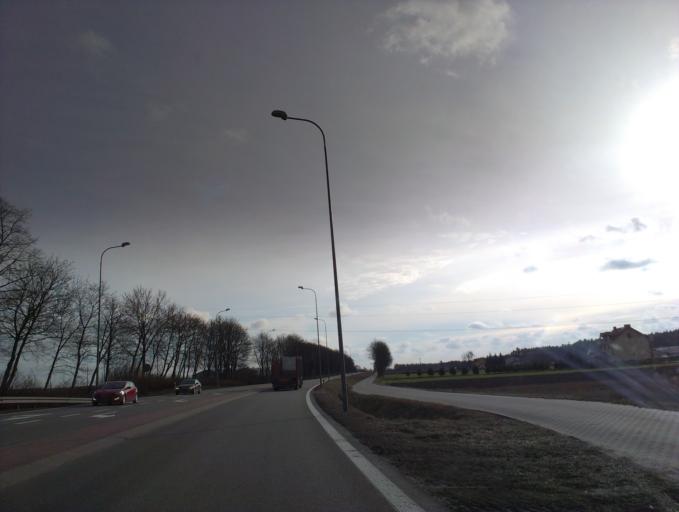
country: PL
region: Kujawsko-Pomorskie
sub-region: Powiat lipnowski
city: Lipno
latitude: 52.8706
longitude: 19.1528
